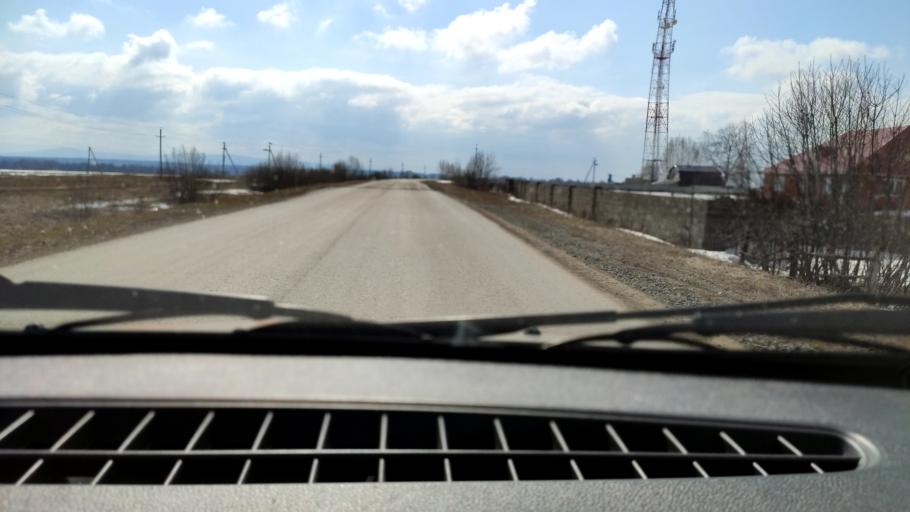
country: RU
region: Bashkortostan
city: Kudeyevskiy
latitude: 54.8444
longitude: 56.7954
